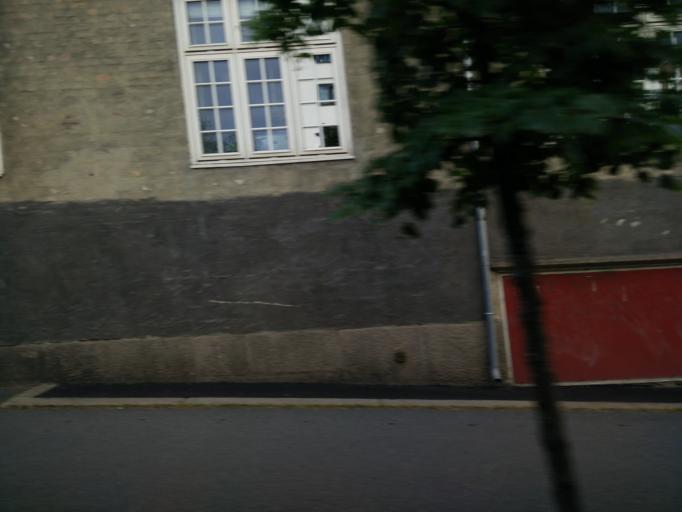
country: NO
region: Oslo
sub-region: Oslo
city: Oslo
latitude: 59.9330
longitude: 10.7256
